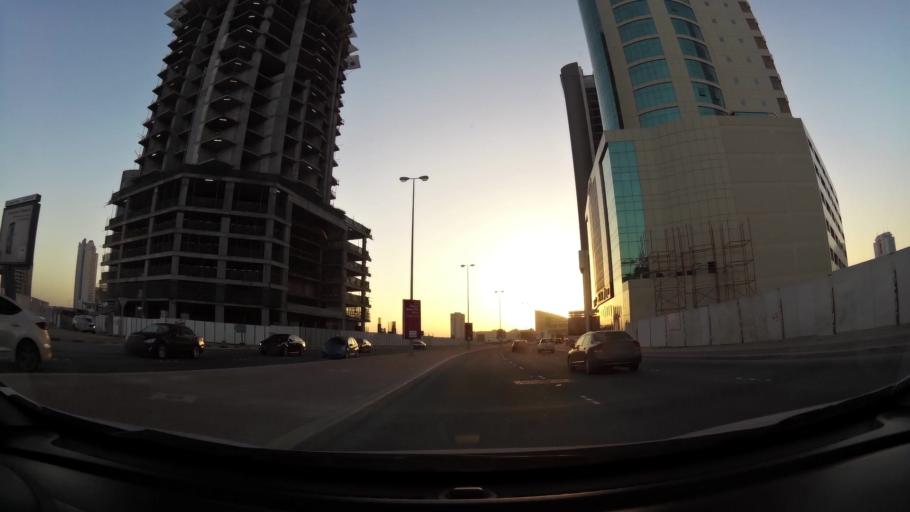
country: BH
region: Manama
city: Jidd Hafs
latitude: 26.2350
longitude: 50.5500
